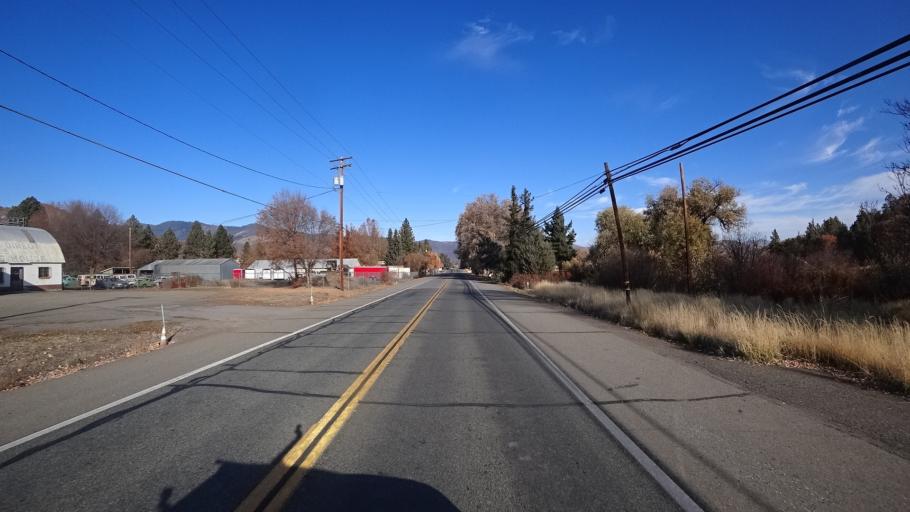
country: US
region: California
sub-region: Siskiyou County
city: Yreka
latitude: 41.7002
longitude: -122.6400
